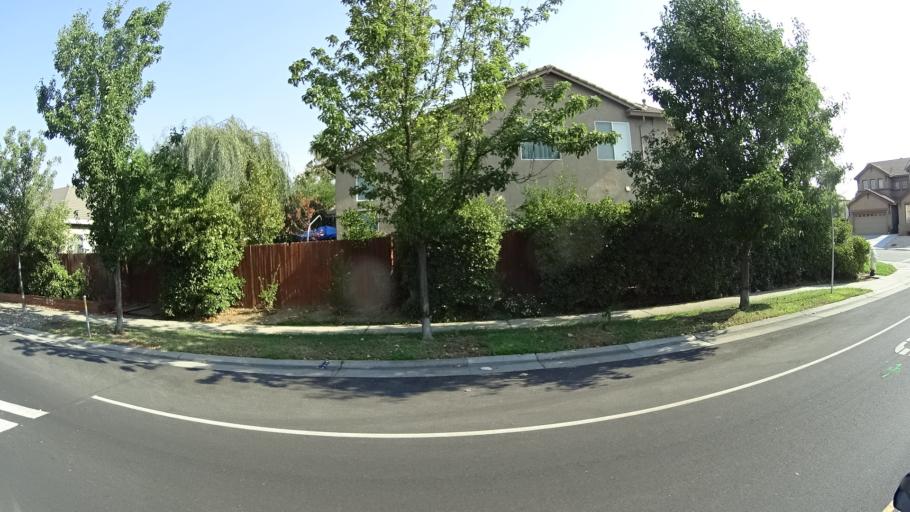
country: US
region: California
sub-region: Sacramento County
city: Laguna
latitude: 38.3892
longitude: -121.4440
